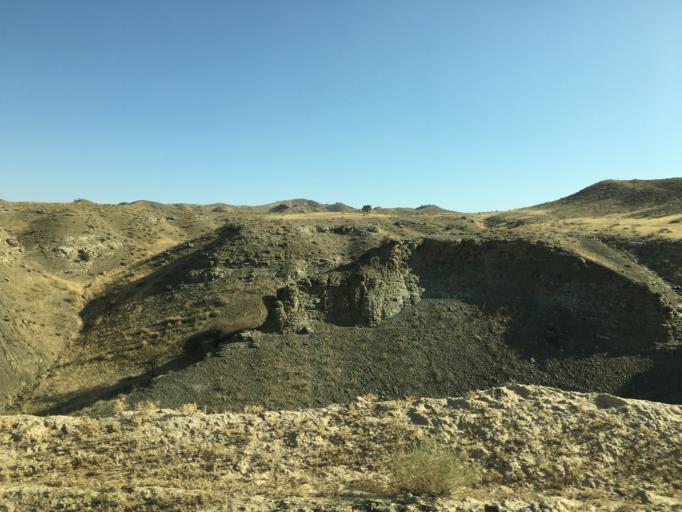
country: TM
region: Balkan
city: Magtymguly
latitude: 38.3009
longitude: 56.7821
